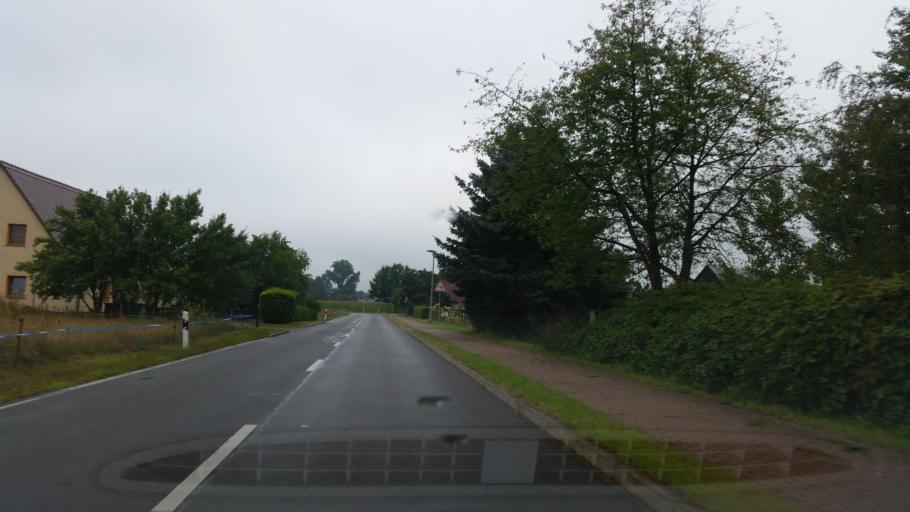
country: DE
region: Brandenburg
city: Tschernitz
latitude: 51.5684
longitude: 14.6128
